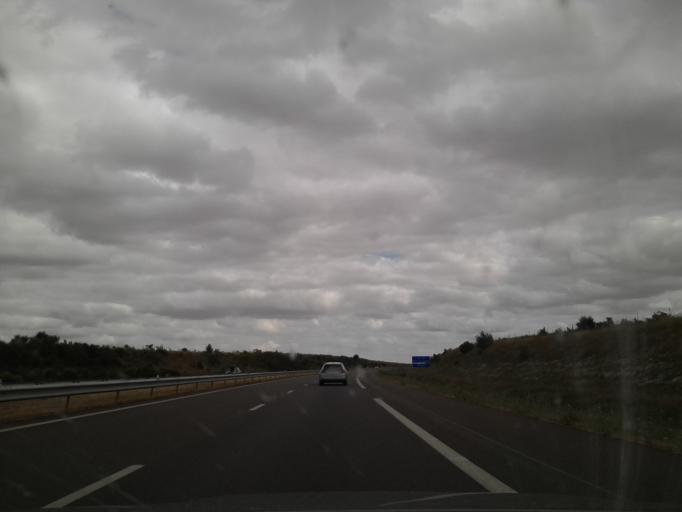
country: FR
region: Centre
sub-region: Departement du Cher
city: Trouy
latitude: 47.0028
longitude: 2.4006
